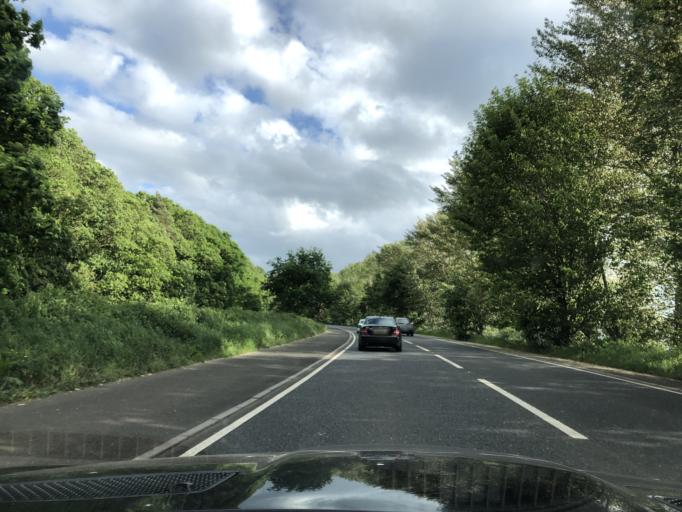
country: GB
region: Northern Ireland
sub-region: Antrim Borough
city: Antrim
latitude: 54.6922
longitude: -6.2270
